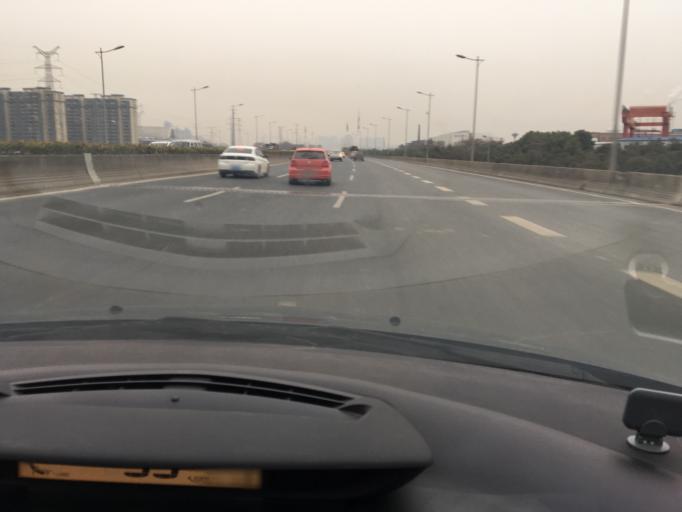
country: CN
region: Hubei
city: Hongqi
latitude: 30.6002
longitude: 114.4269
